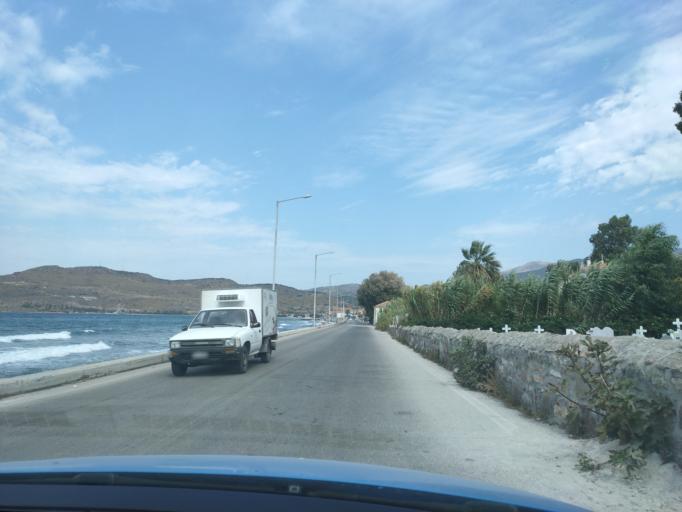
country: GR
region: North Aegean
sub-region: Nomos Lesvou
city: Petra
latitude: 39.3240
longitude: 26.1693
